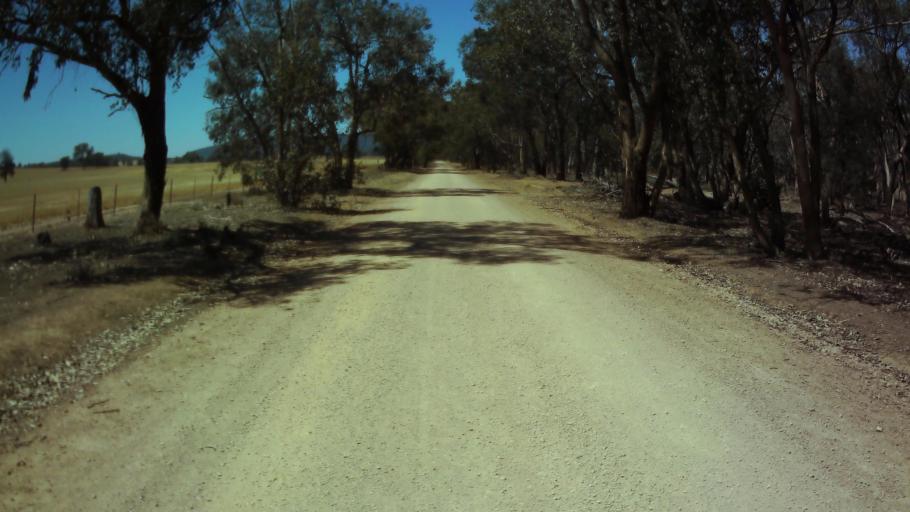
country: AU
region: New South Wales
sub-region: Weddin
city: Grenfell
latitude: -33.9133
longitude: 148.0796
